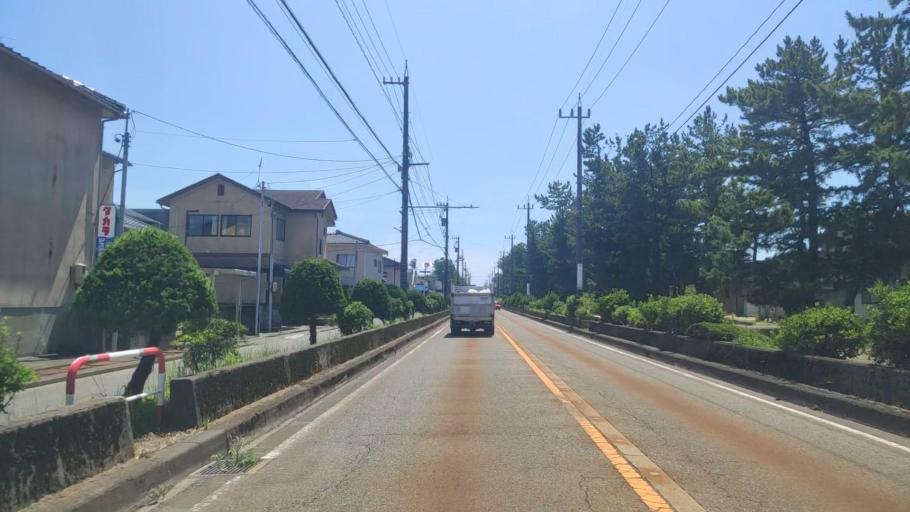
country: JP
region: Ishikawa
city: Kanazawa-shi
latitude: 36.6289
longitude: 136.6232
